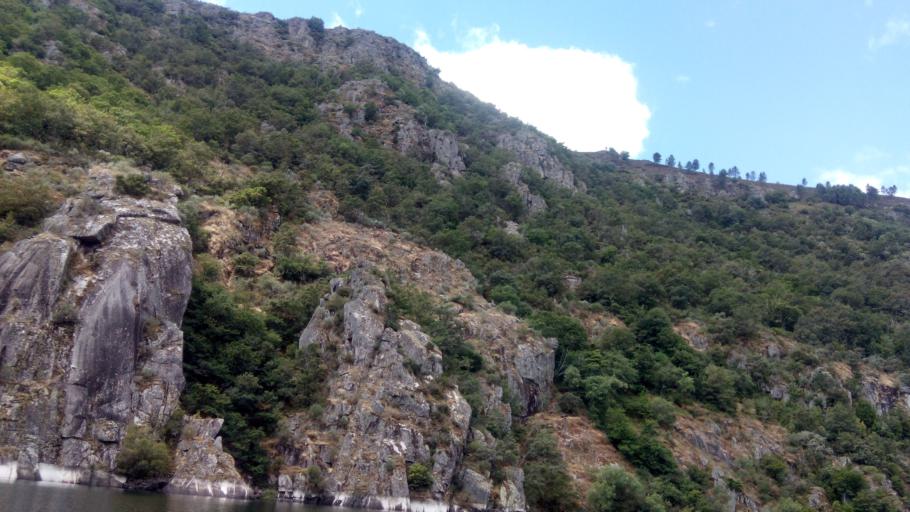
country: ES
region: Galicia
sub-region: Provincia de Lugo
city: Sober
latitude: 42.3947
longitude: -7.6264
